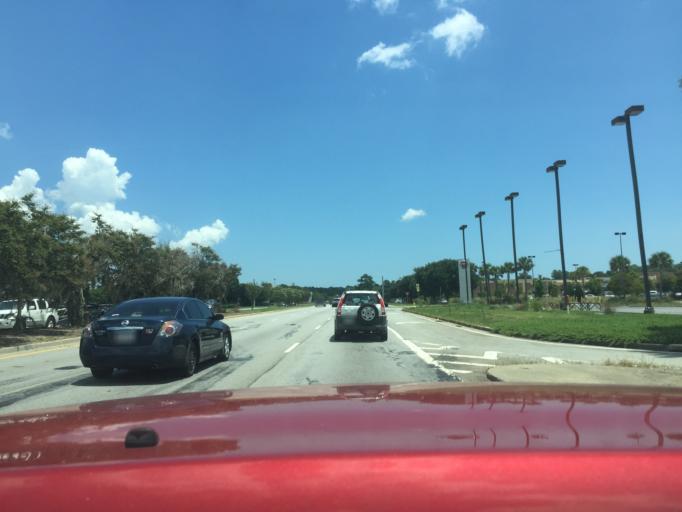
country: US
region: Georgia
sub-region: Chatham County
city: Georgetown
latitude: 31.9825
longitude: -81.1761
